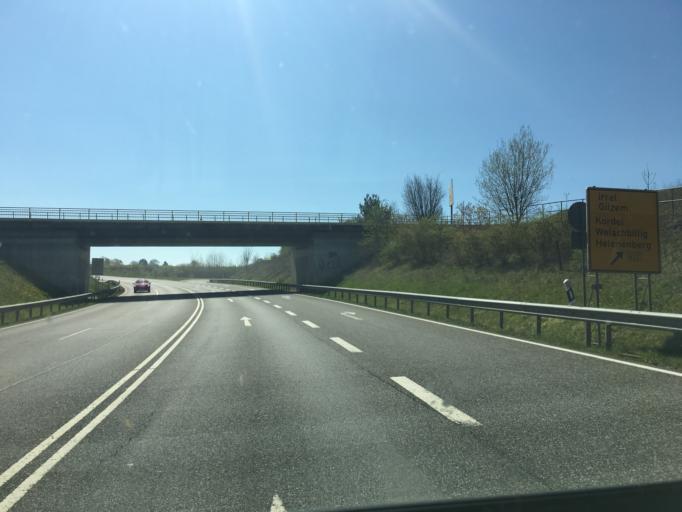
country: DE
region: Rheinland-Pfalz
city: Eisenach
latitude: 49.8570
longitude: 6.5414
